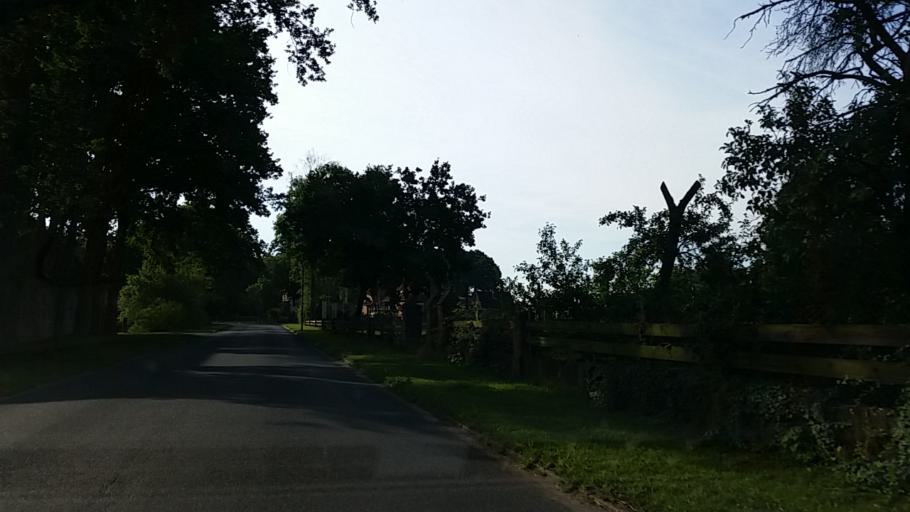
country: DE
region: Lower Saxony
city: Wieren
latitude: 52.9110
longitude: 10.6607
